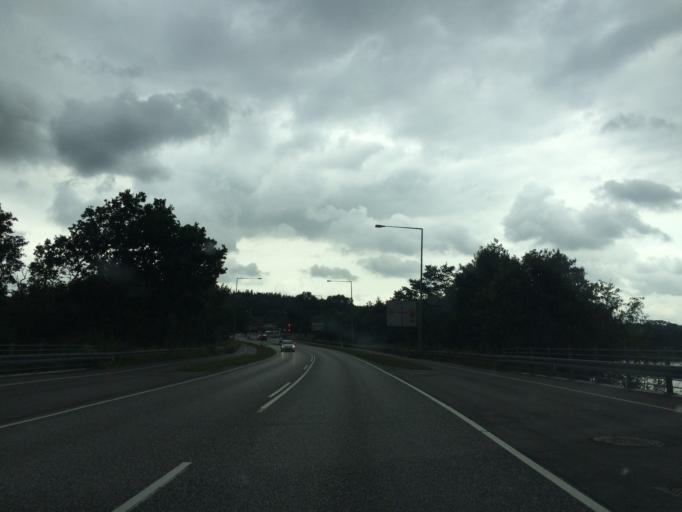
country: DK
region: Central Jutland
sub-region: Silkeborg Kommune
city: Silkeborg
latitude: 56.1725
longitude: 9.5278
